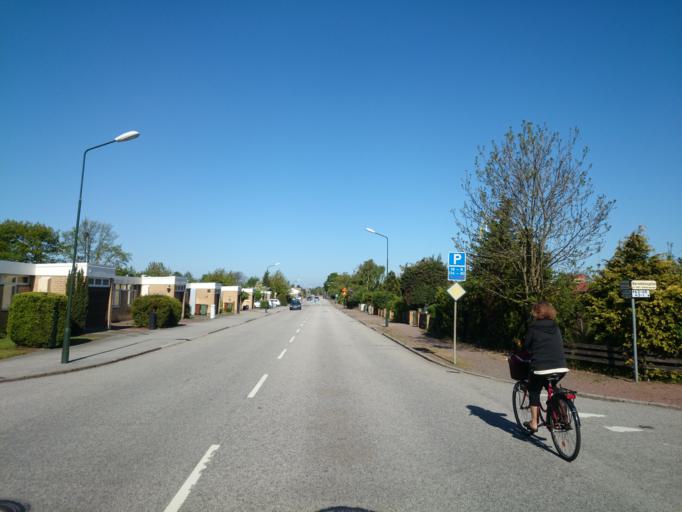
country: SE
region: Skane
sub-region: Malmo
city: Malmoe
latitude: 55.5773
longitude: 12.9694
